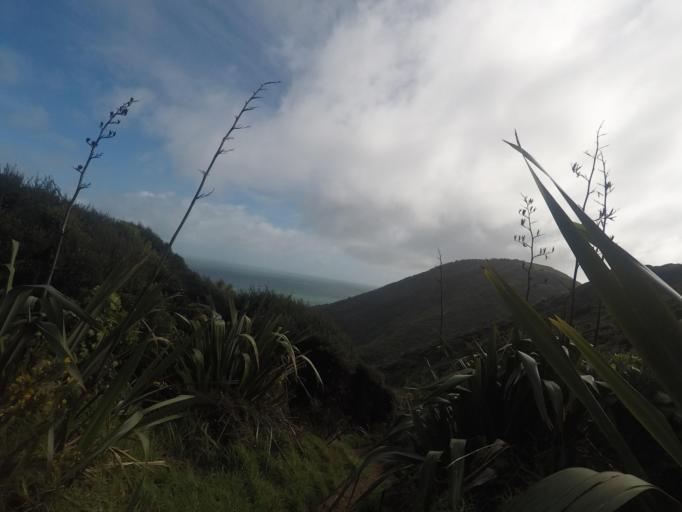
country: NZ
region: Auckland
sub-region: Auckland
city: Muriwai Beach
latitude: -36.8578
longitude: 174.4341
